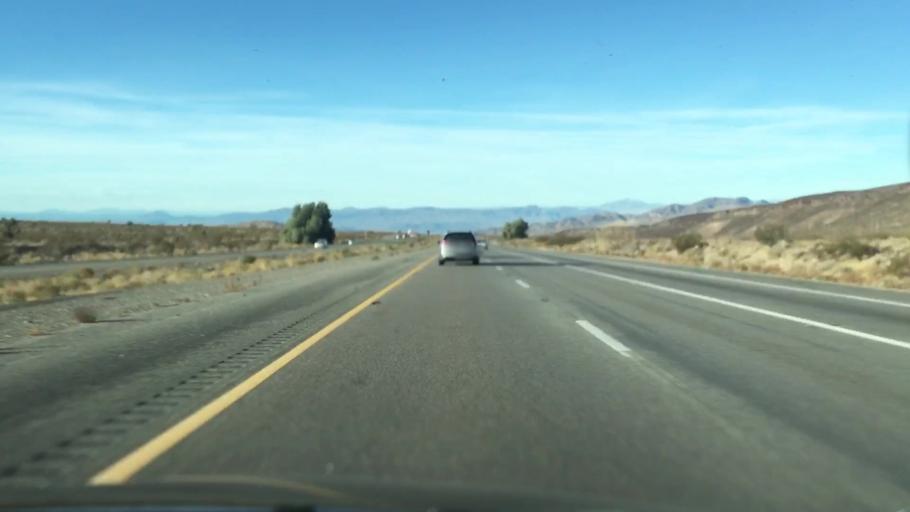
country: US
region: Nevada
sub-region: Clark County
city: Sandy Valley
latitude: 35.3907
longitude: -115.8392
